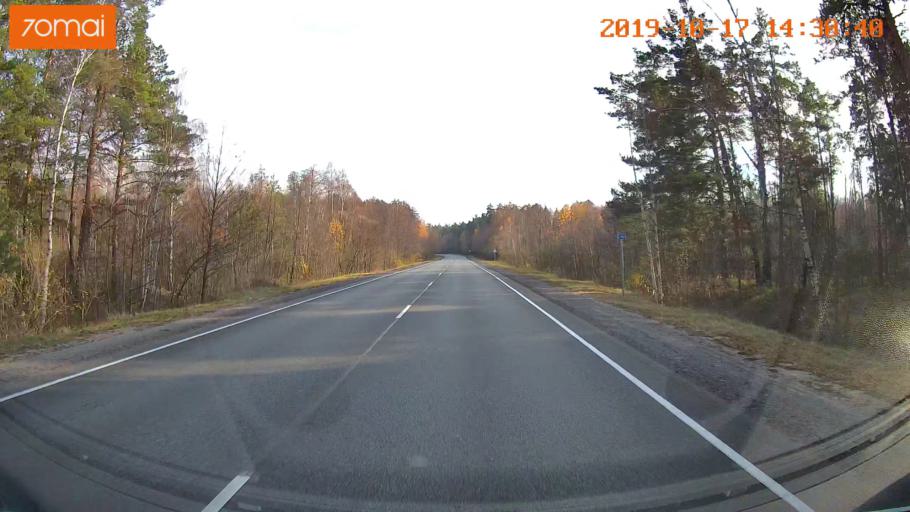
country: RU
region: Rjazan
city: Solotcha
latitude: 54.9446
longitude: 39.9487
